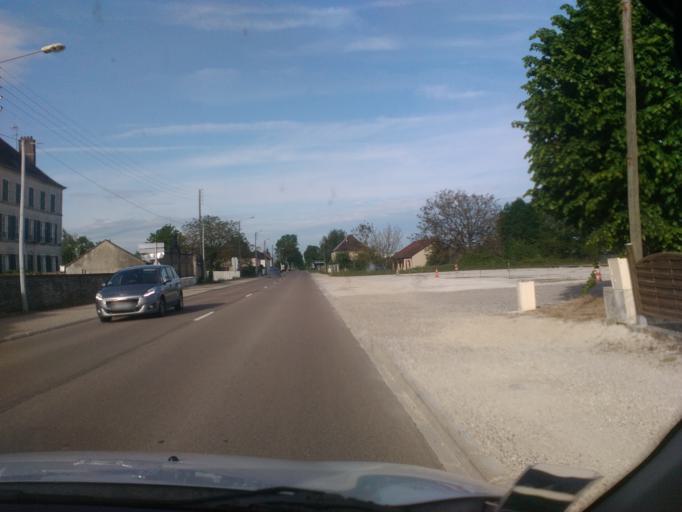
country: FR
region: Champagne-Ardenne
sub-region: Departement de l'Aube
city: Vendeuvre-sur-Barse
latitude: 48.2409
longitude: 4.5333
